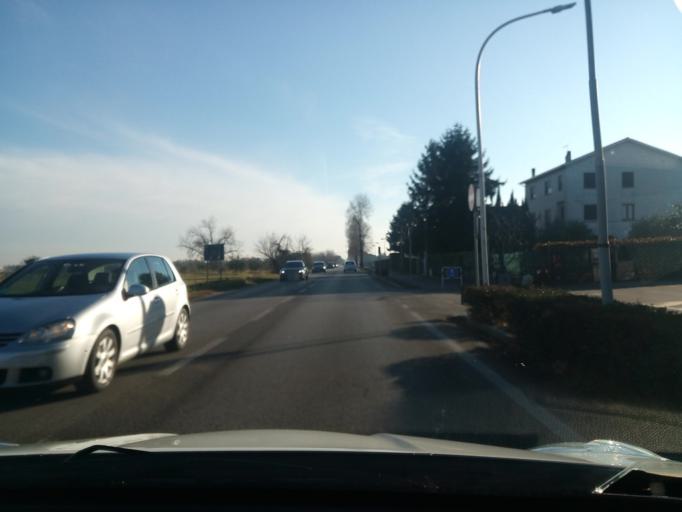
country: IT
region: Veneto
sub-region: Provincia di Vicenza
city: Thiene
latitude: 45.6819
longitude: 11.4852
